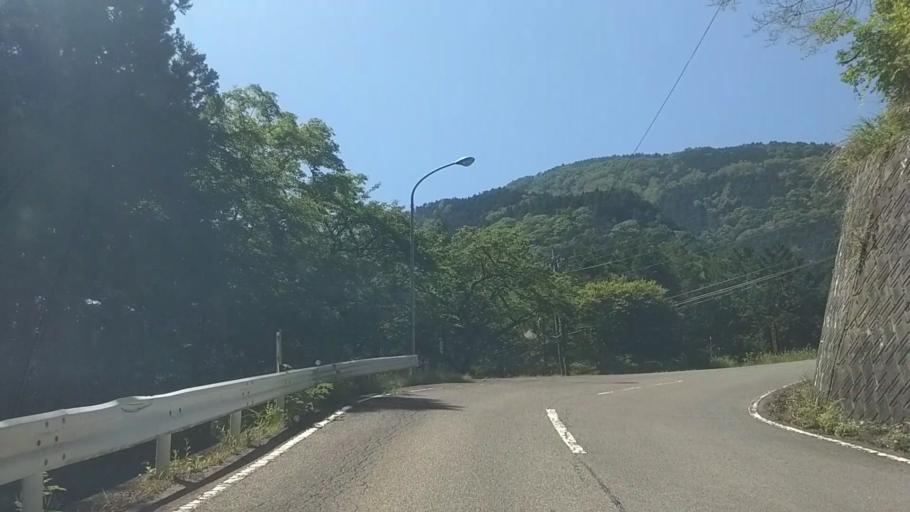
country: JP
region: Yamanashi
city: Ryuo
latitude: 35.5098
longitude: 138.4051
